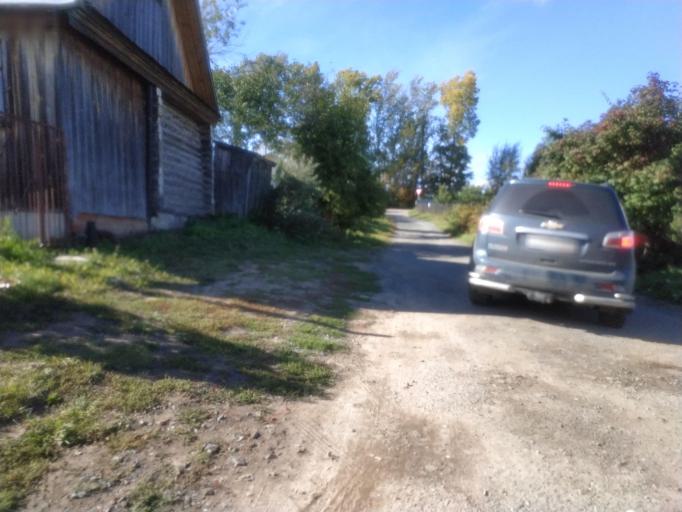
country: RU
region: Chuvashia
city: Novyye Lapsary
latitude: 56.1421
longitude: 47.1457
